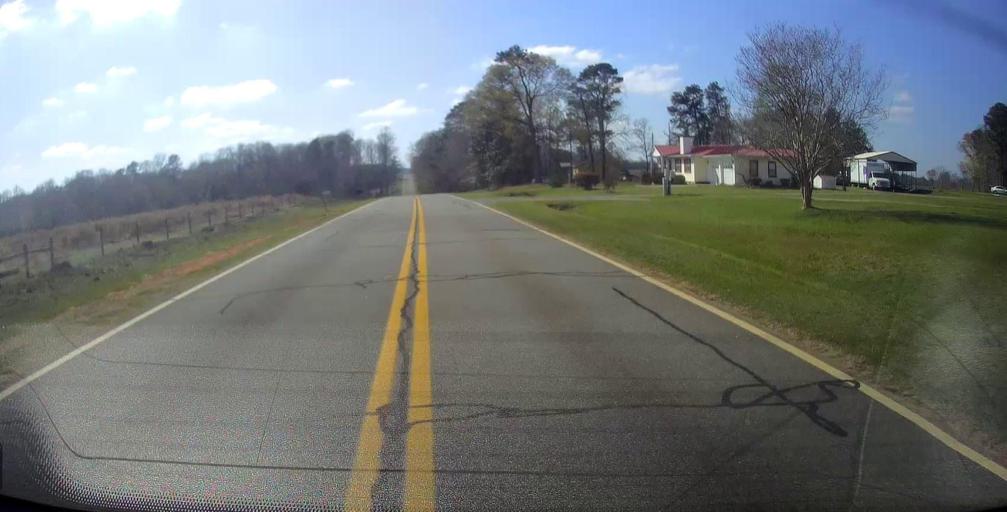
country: US
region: Georgia
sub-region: Twiggs County
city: Jeffersonville
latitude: 32.6812
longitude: -83.2966
